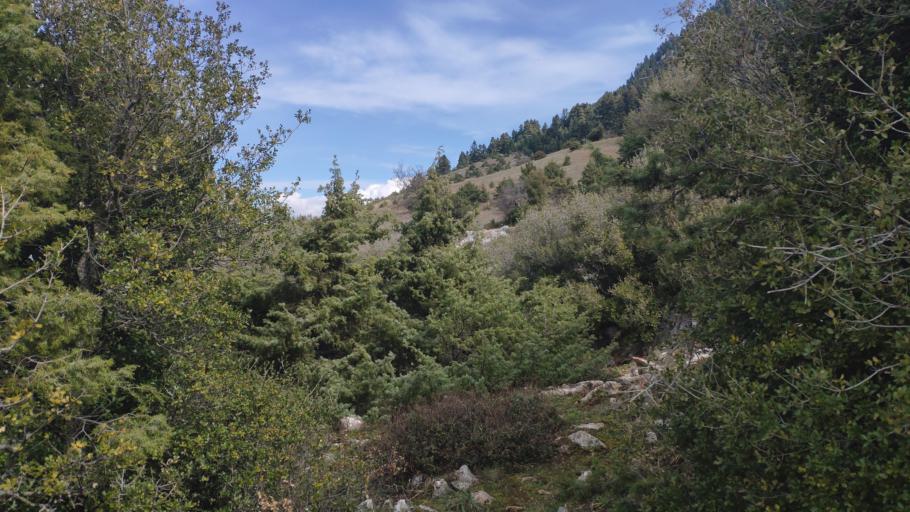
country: GR
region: Central Greece
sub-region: Nomos Fokidos
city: Amfissa
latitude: 38.6451
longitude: 22.4244
